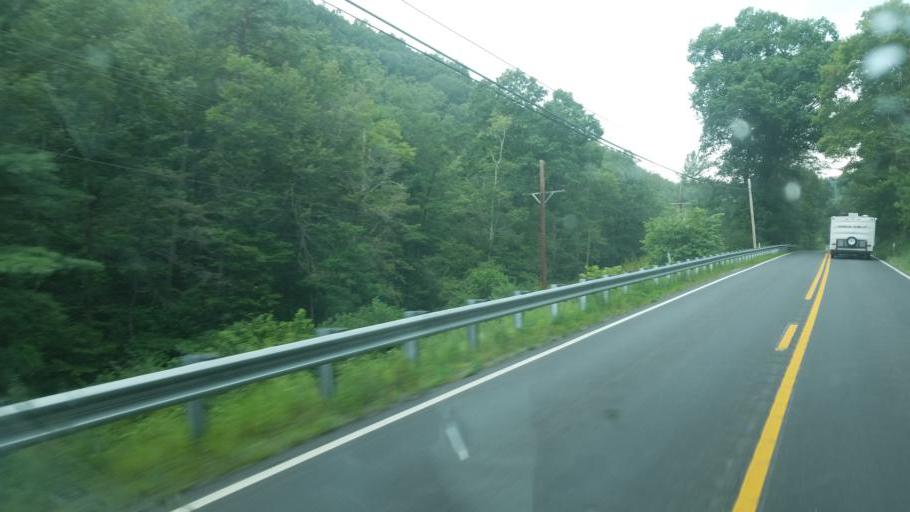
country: US
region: West Virginia
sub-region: Mineral County
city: Fort Ashby
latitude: 39.5471
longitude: -78.5553
